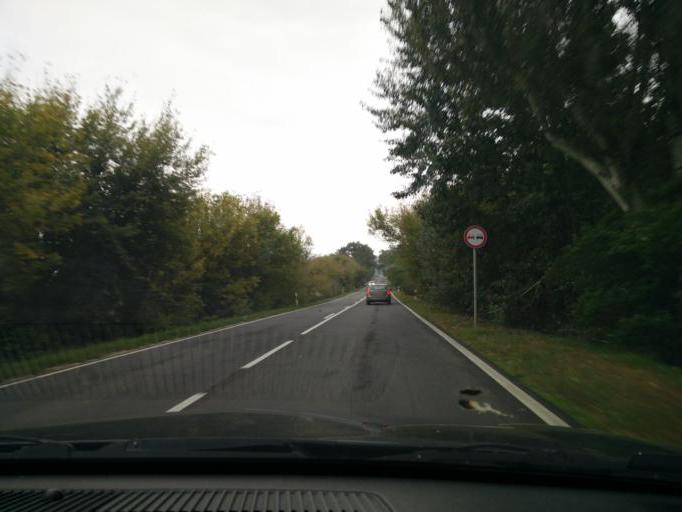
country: HU
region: Komarom-Esztergom
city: Kesztolc
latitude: 47.7072
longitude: 18.7680
